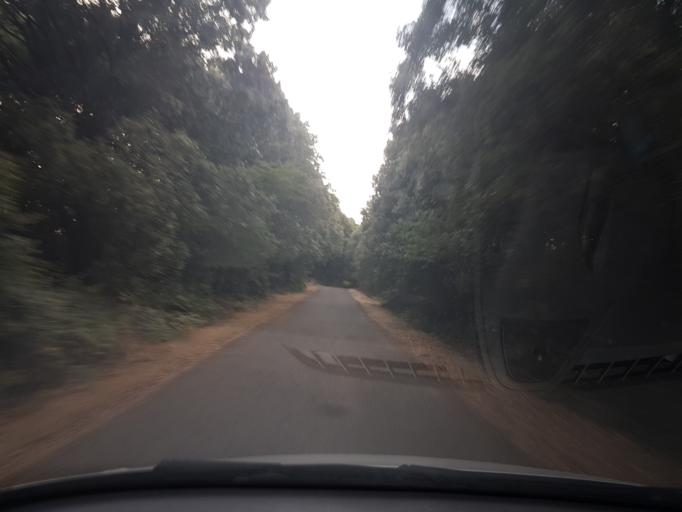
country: IT
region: Sardinia
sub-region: Provincia di Oristano
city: Seneghe
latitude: 40.1103
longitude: 8.5857
